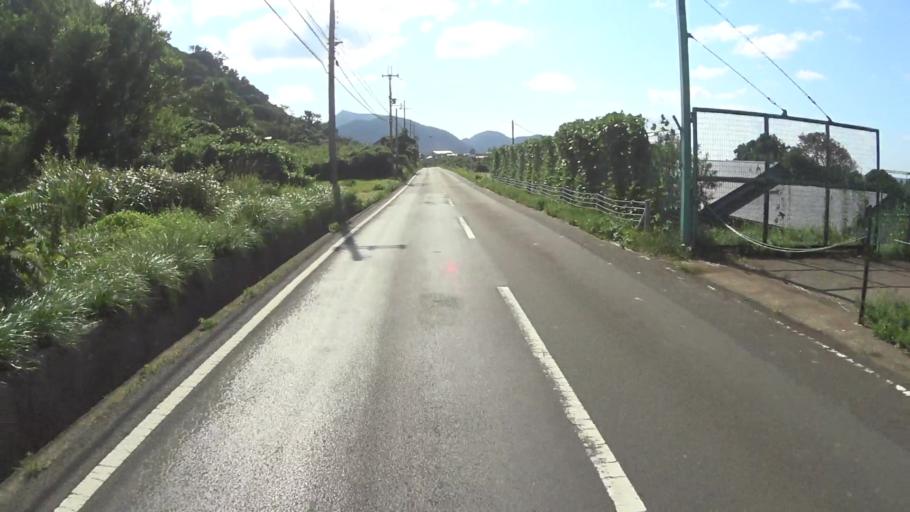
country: JP
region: Kyoto
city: Miyazu
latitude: 35.7607
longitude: 135.1862
